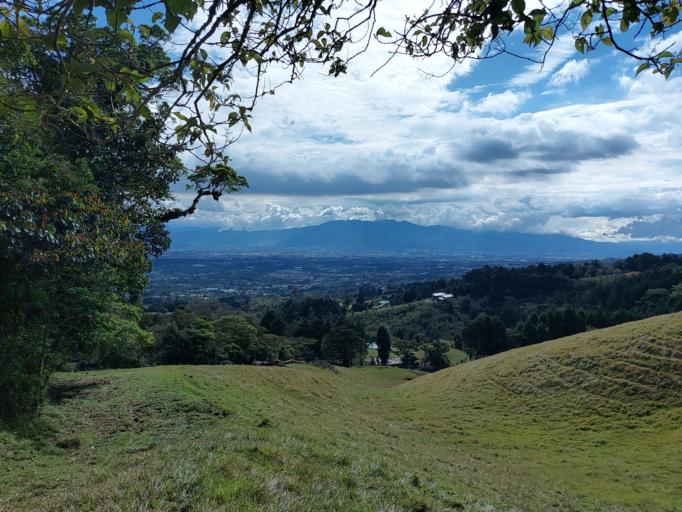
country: CR
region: Heredia
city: Angeles
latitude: 10.0451
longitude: -84.0285
